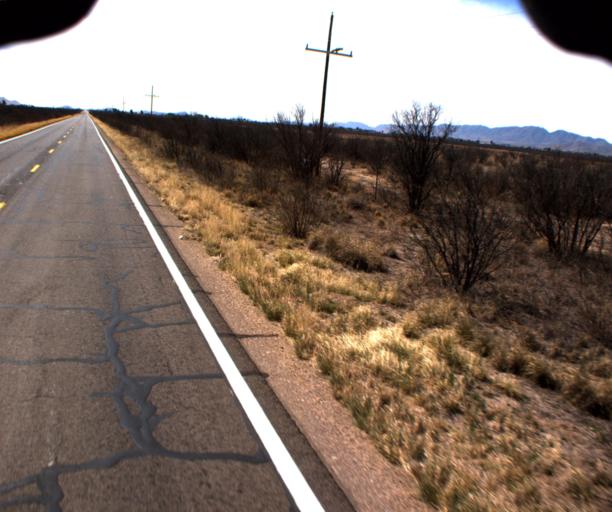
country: US
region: Arizona
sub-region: Cochise County
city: Willcox
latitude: 32.0247
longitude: -109.8733
